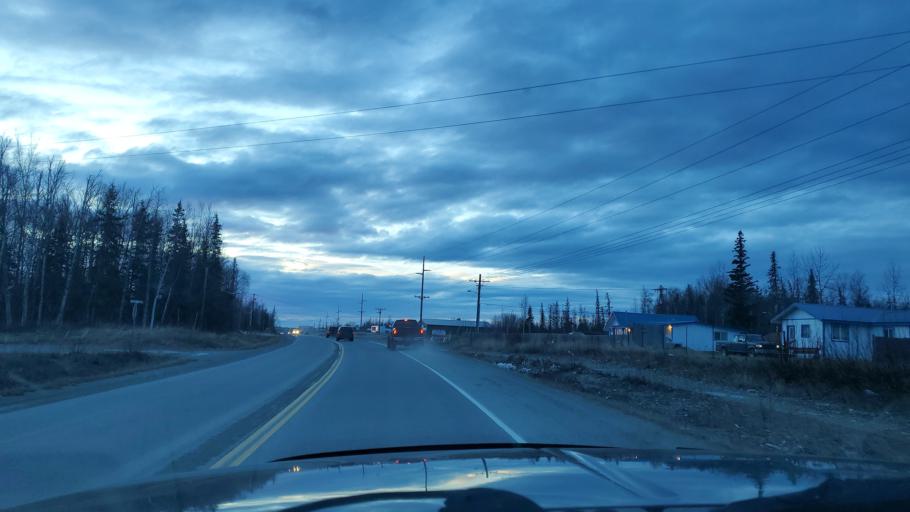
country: US
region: Alaska
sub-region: Matanuska-Susitna Borough
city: Wasilla
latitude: 61.5929
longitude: -149.3924
